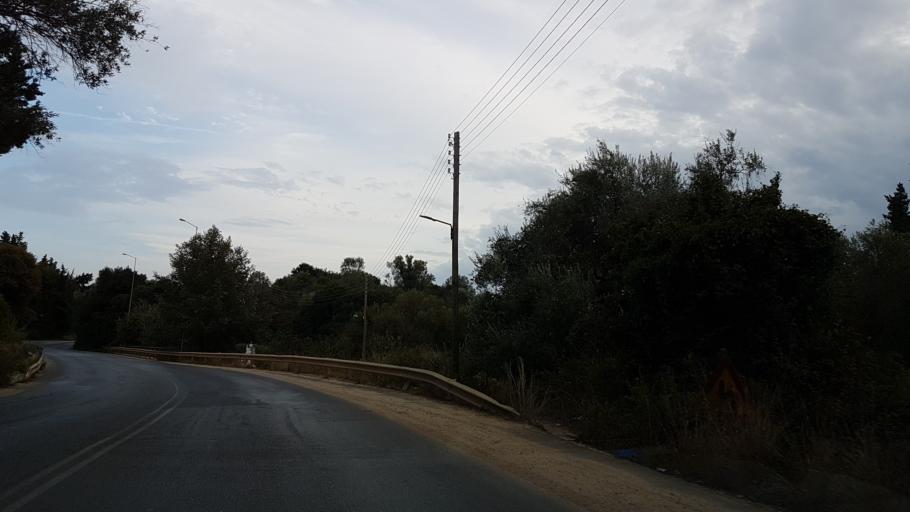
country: GR
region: Ionian Islands
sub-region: Nomos Kerkyras
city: Kontokali
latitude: 39.6711
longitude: 19.8398
